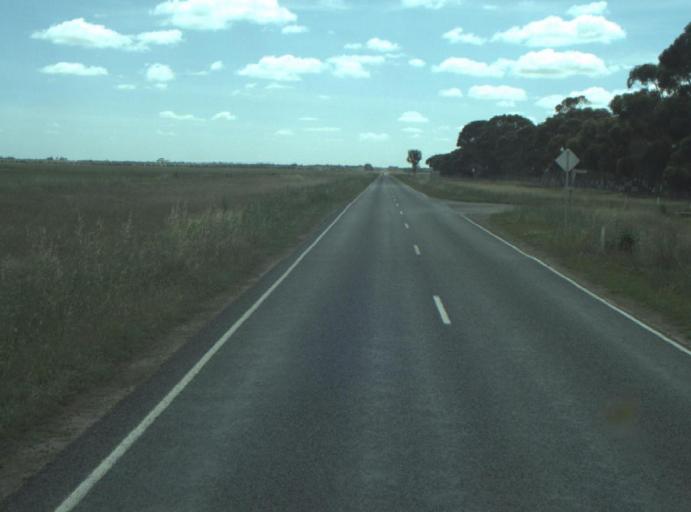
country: AU
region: Victoria
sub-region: Greater Geelong
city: Lara
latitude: -38.0138
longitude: 144.4530
